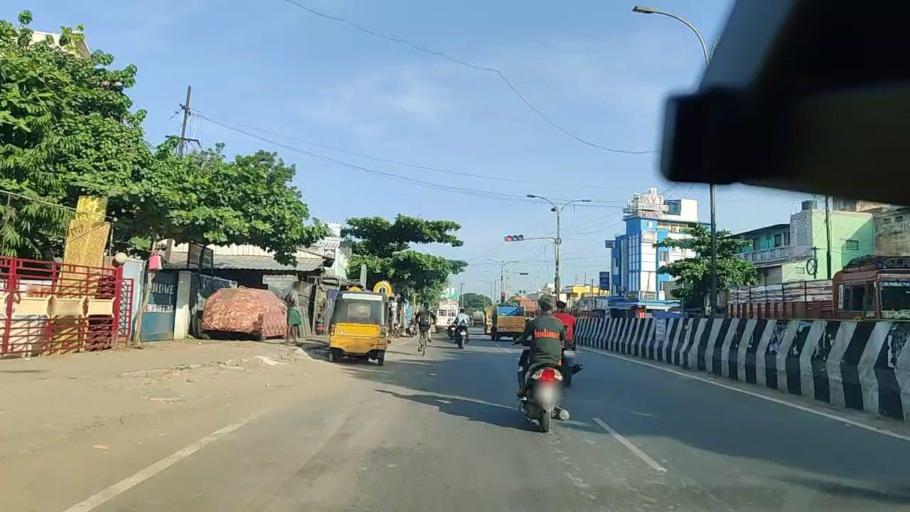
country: IN
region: Tamil Nadu
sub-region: Thiruvallur
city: Chinnasekkadu
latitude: 13.1232
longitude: 80.2487
